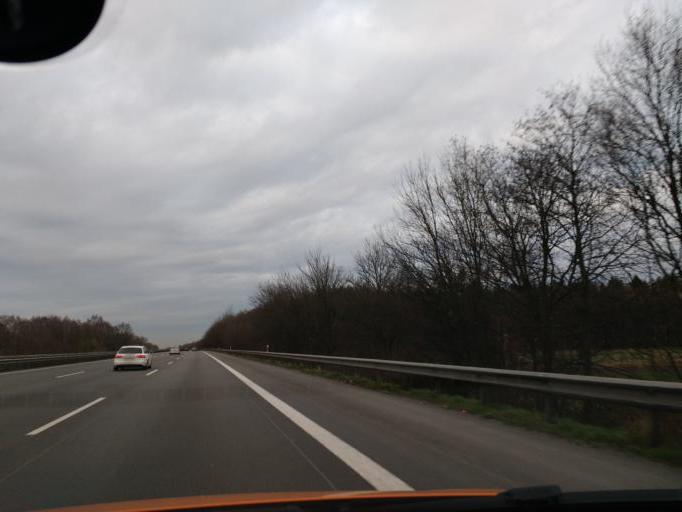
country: DE
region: Lower Saxony
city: Hademstorf
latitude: 52.7237
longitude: 9.6798
